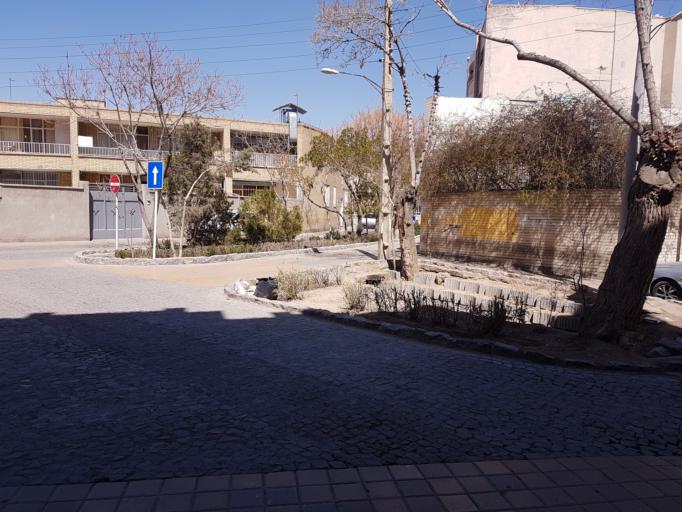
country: IR
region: Isfahan
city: Isfahan
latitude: 32.6315
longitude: 51.6518
